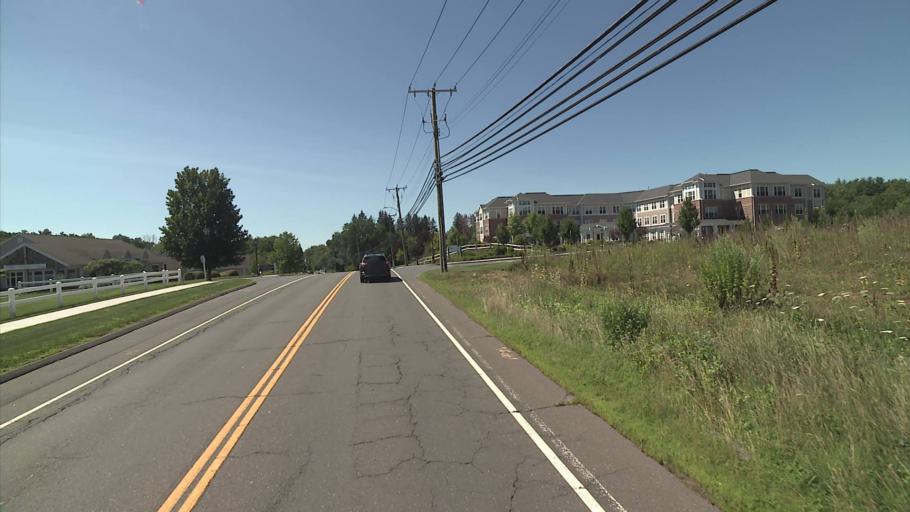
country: US
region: Connecticut
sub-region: Hartford County
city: Weatogue
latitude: 41.8185
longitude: -72.8298
